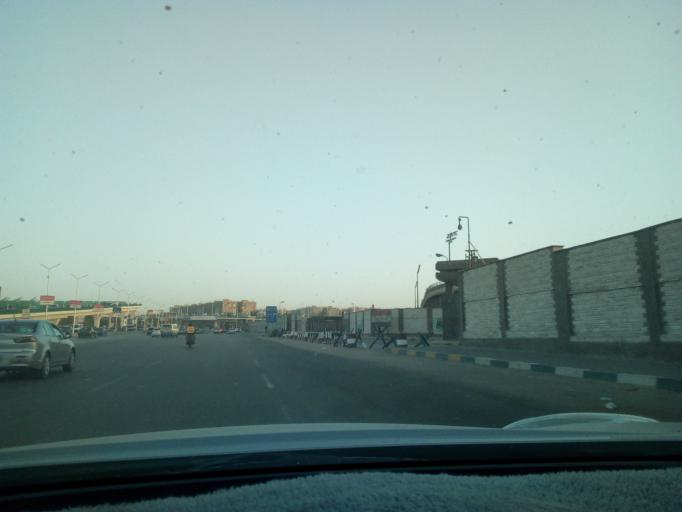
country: EG
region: Muhafazat al Qalyubiyah
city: Al Khankah
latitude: 30.1131
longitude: 31.3677
